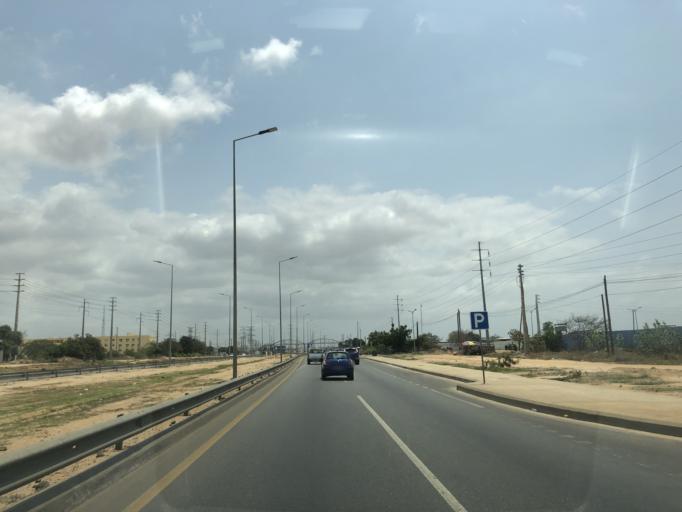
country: AO
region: Luanda
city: Luanda
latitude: -8.9632
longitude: 13.2562
